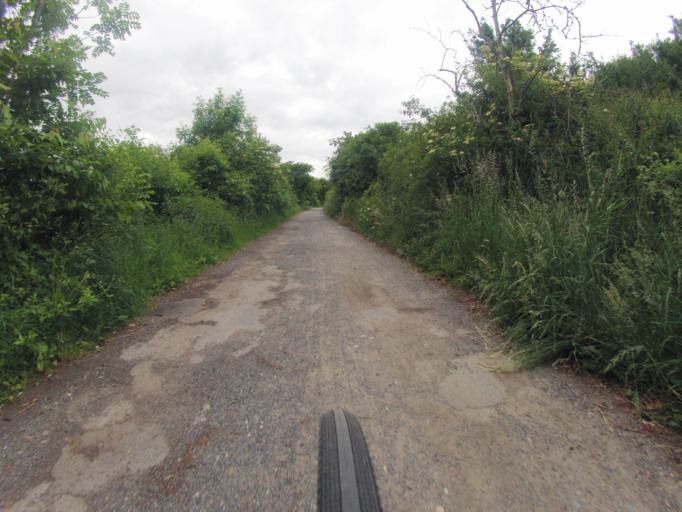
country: DE
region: North Rhine-Westphalia
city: Ibbenburen
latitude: 52.2269
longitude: 7.7324
